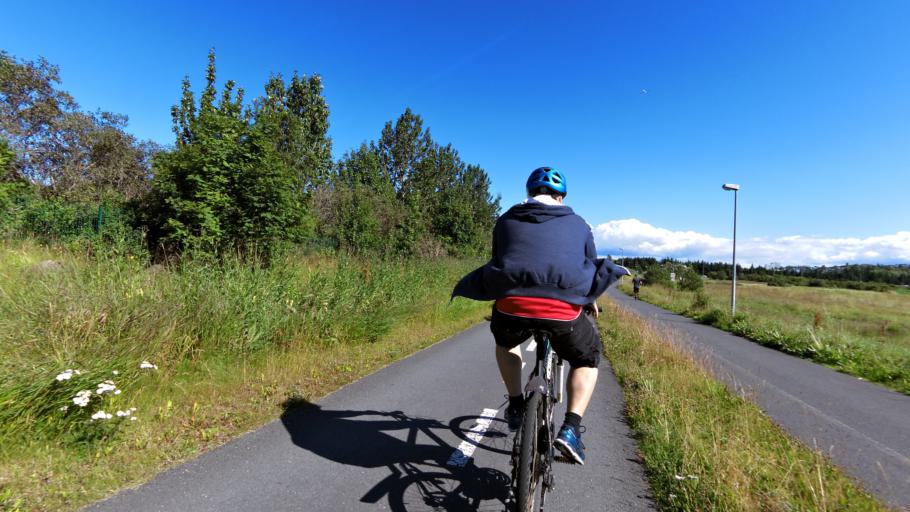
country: IS
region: Capital Region
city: Kopavogur
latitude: 64.1208
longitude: -21.9067
